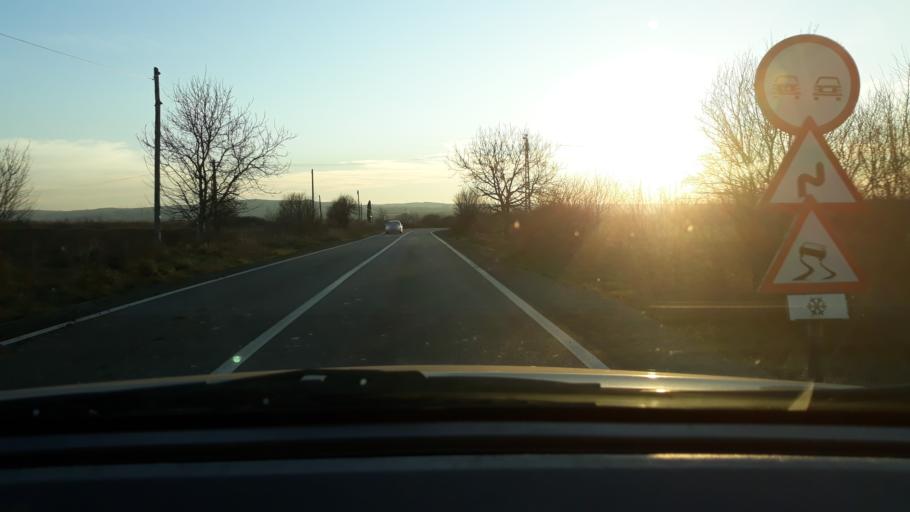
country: RO
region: Bihor
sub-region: Comuna Spinus
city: Spinus
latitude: 47.2387
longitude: 22.1951
